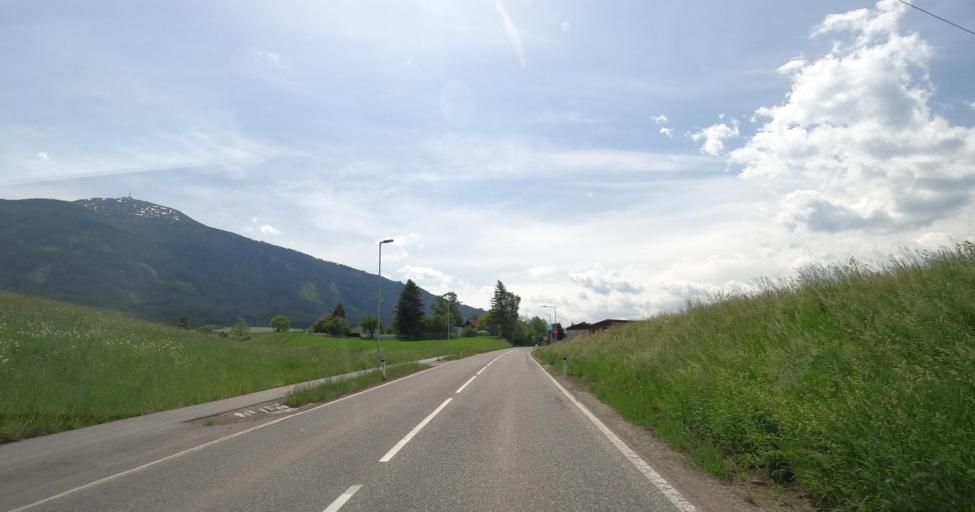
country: AT
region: Tyrol
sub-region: Politischer Bezirk Innsbruck Land
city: Aldrans
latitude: 47.2423
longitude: 11.4364
